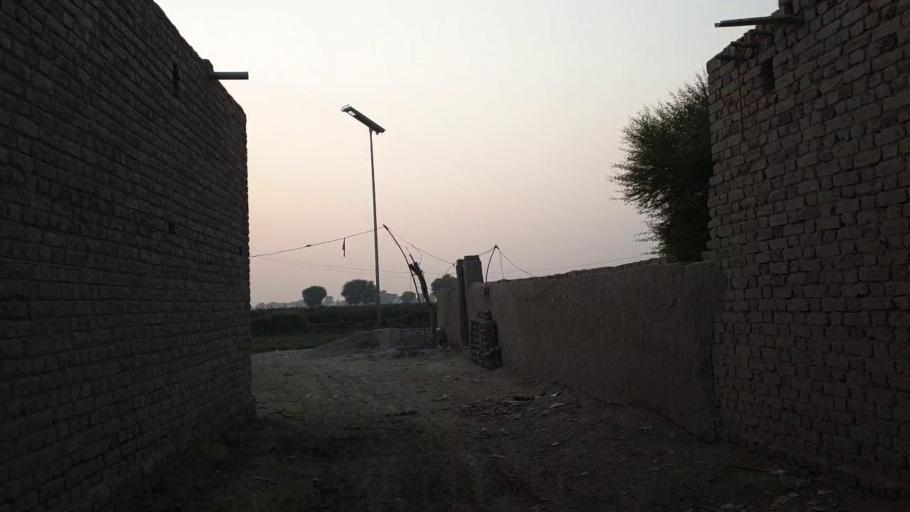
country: PK
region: Sindh
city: Bhan
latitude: 26.5259
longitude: 67.7096
